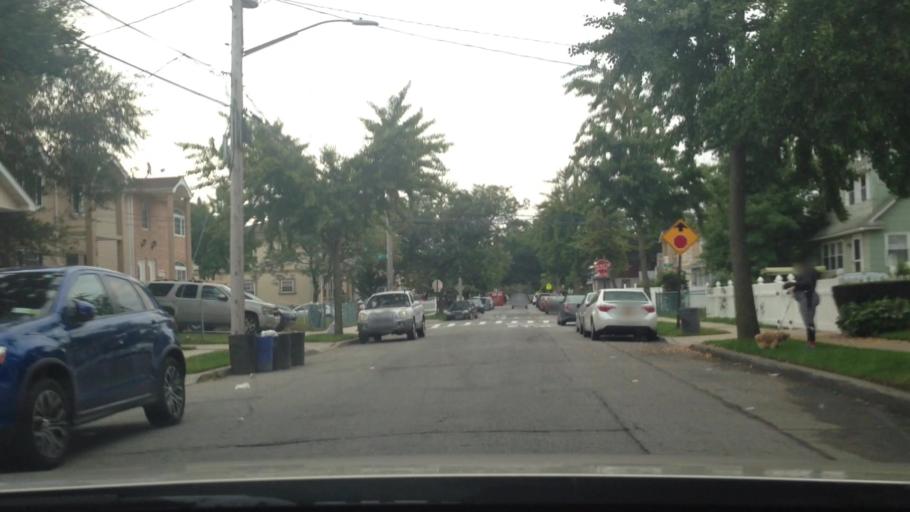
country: US
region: New York
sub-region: Nassau County
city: South Valley Stream
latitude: 40.6623
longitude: -73.7351
